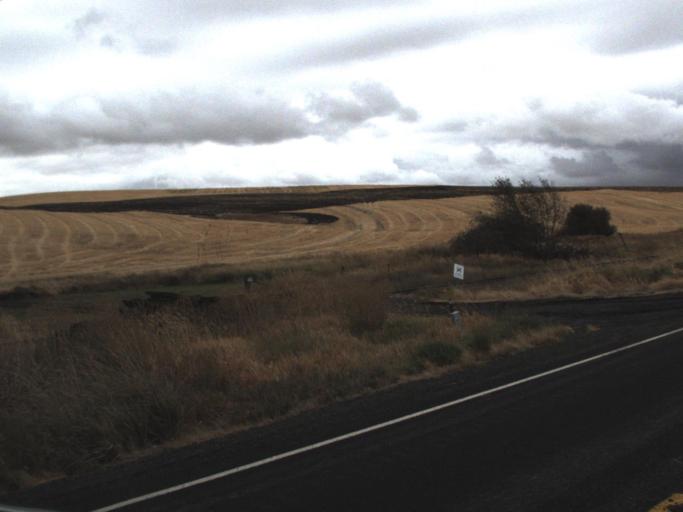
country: US
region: Washington
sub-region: Whitman County
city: Colfax
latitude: 47.1975
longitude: -117.3446
